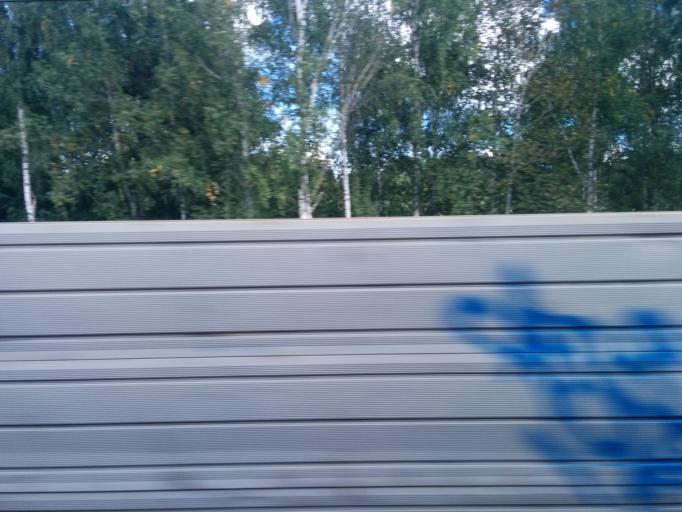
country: RU
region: Moskovskaya
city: Sheremet'yevskiy
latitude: 55.9875
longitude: 37.4973
